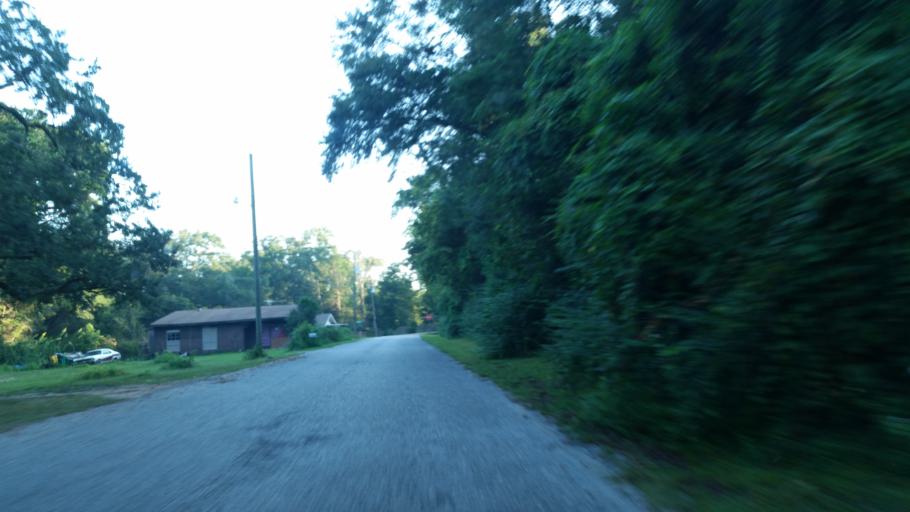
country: US
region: Florida
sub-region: Escambia County
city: Ferry Pass
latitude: 30.5322
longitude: -87.2023
